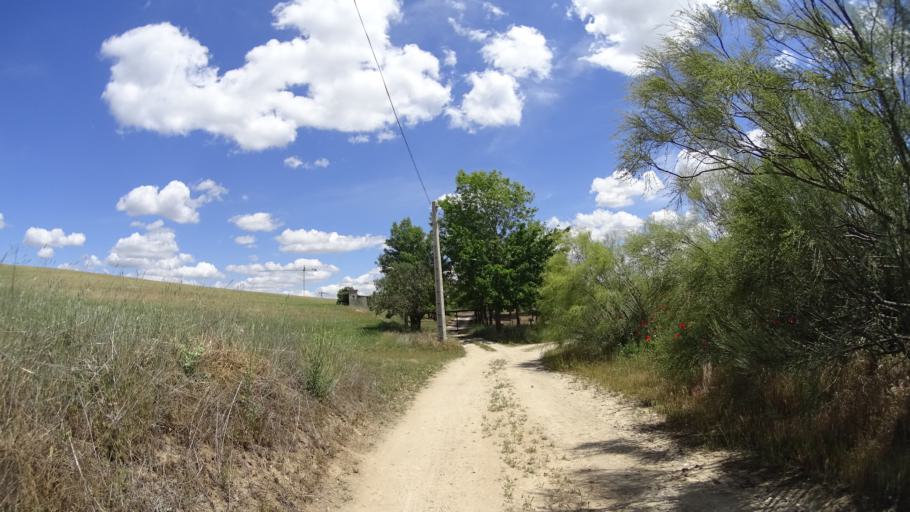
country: ES
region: Madrid
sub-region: Provincia de Madrid
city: Boadilla del Monte
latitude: 40.4121
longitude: -3.9216
